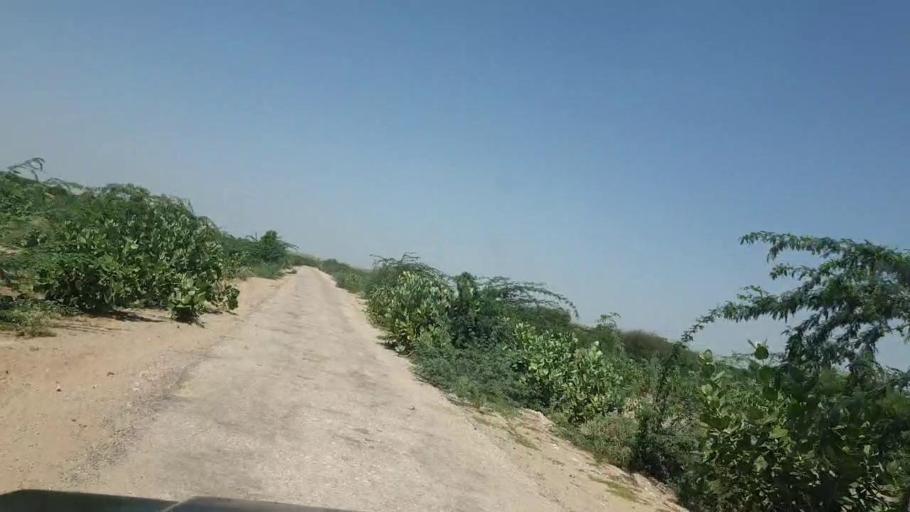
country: PK
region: Sindh
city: Chor
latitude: 25.4005
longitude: 70.3110
